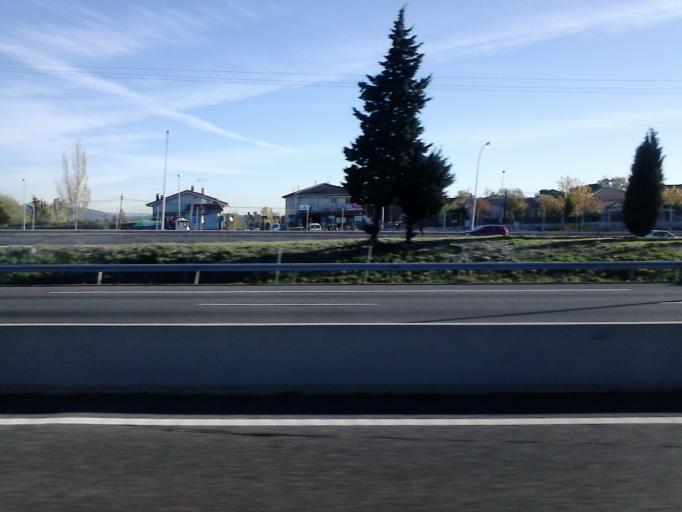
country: ES
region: Madrid
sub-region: Provincia de Madrid
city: Las Matas
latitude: 40.5595
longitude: -3.9017
